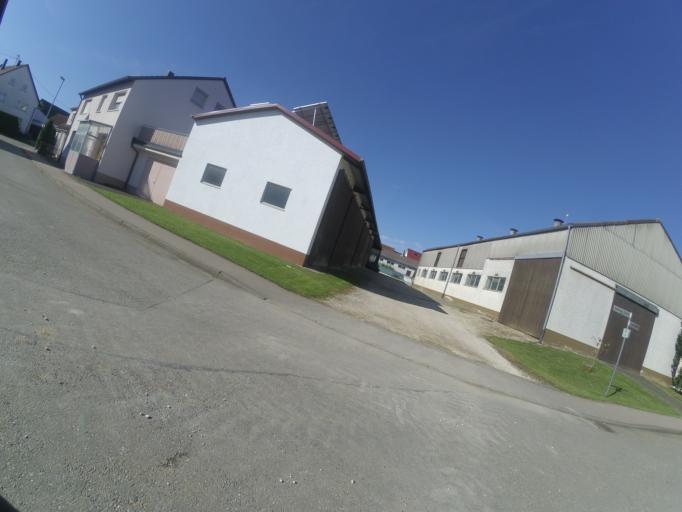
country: DE
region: Baden-Wuerttemberg
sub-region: Tuebingen Region
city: Holzkirch
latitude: 48.5312
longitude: 9.9962
